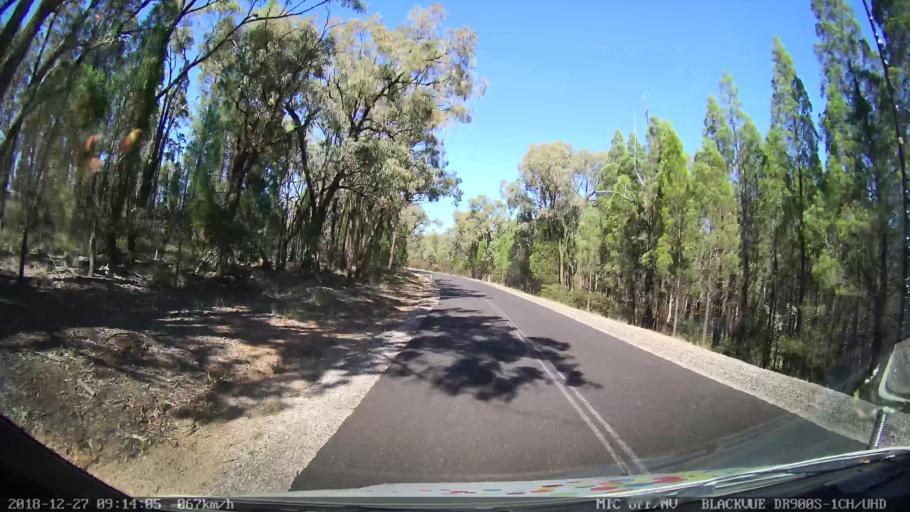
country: AU
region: New South Wales
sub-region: Lithgow
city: Portland
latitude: -33.1371
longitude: 150.0863
